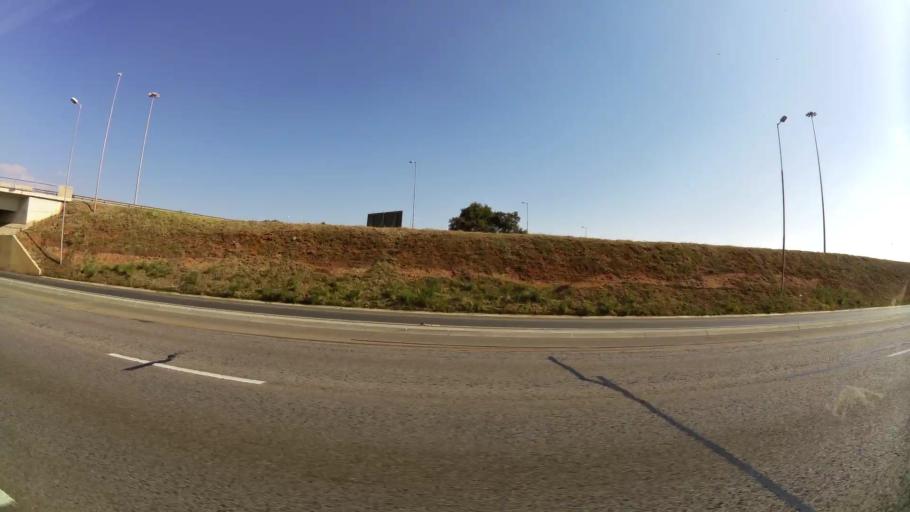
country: ZA
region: Gauteng
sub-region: Ekurhuleni Metropolitan Municipality
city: Tembisa
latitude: -26.0623
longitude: 28.2780
